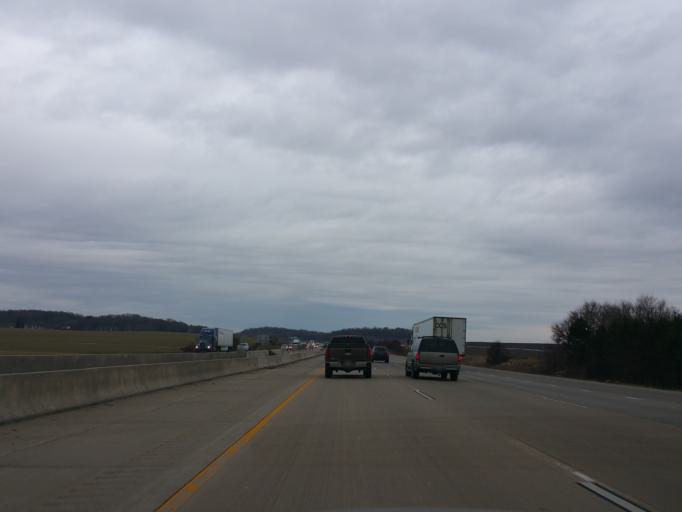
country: US
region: Wisconsin
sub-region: Columbia County
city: Poynette
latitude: 43.3325
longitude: -89.4525
